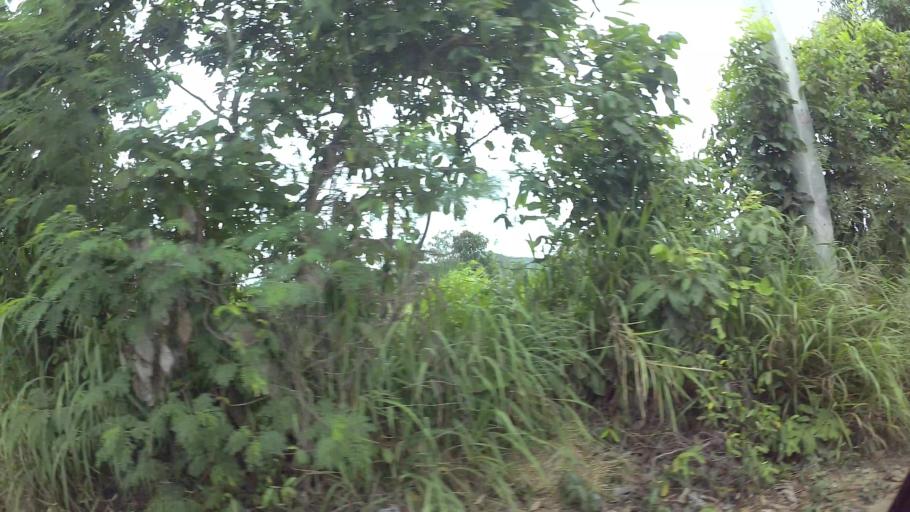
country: TH
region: Chon Buri
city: Si Racha
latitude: 13.1845
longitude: 100.9771
